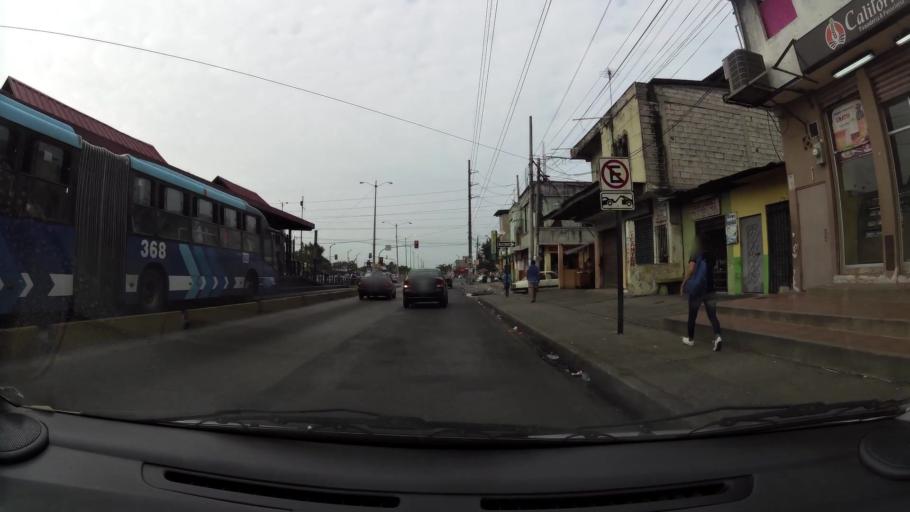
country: EC
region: Guayas
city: Guayaquil
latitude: -2.2503
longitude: -79.8902
